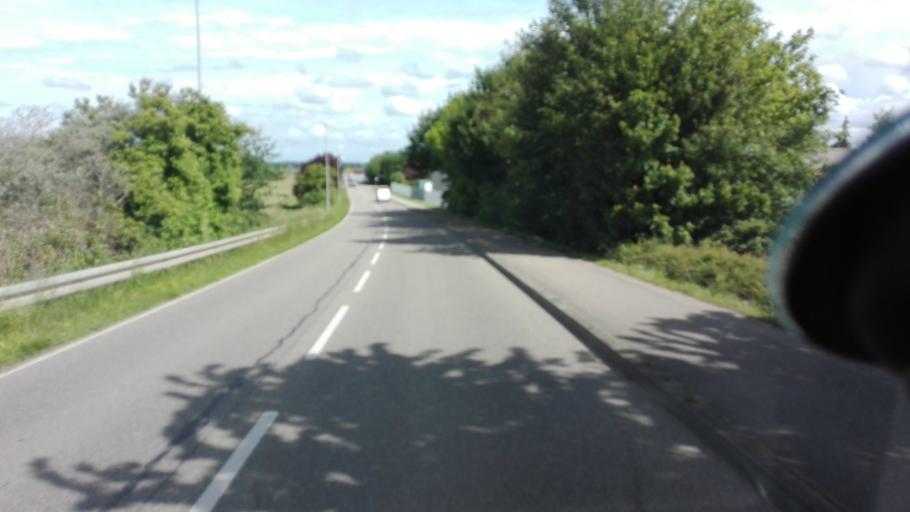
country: DE
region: Baden-Wuerttemberg
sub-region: Karlsruhe Region
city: Karlsdorf-Neuthard
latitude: 49.1458
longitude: 8.5469
